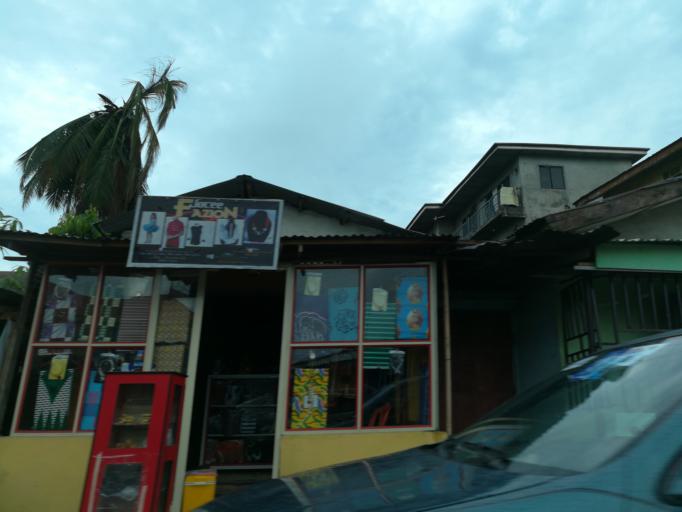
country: NG
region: Rivers
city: Port Harcourt
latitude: 4.8535
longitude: 7.0338
